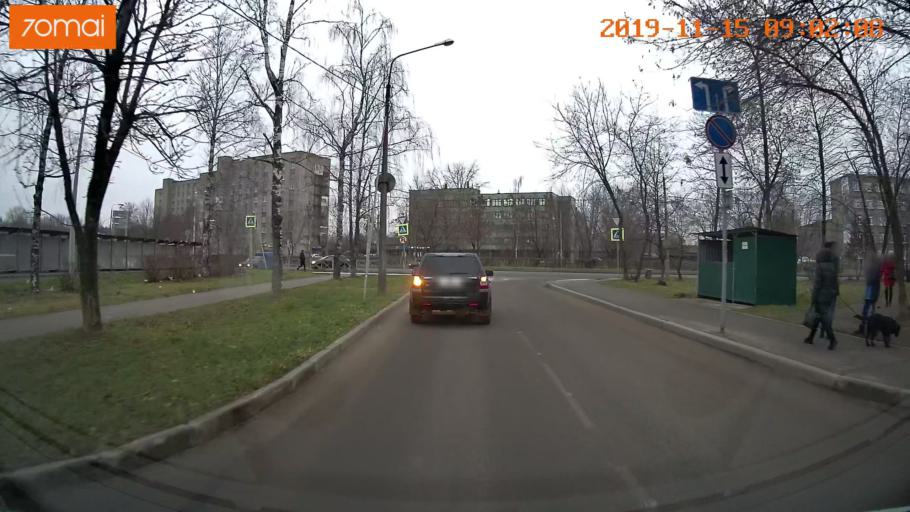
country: RU
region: Vologda
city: Cherepovets
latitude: 59.1360
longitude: 37.9268
